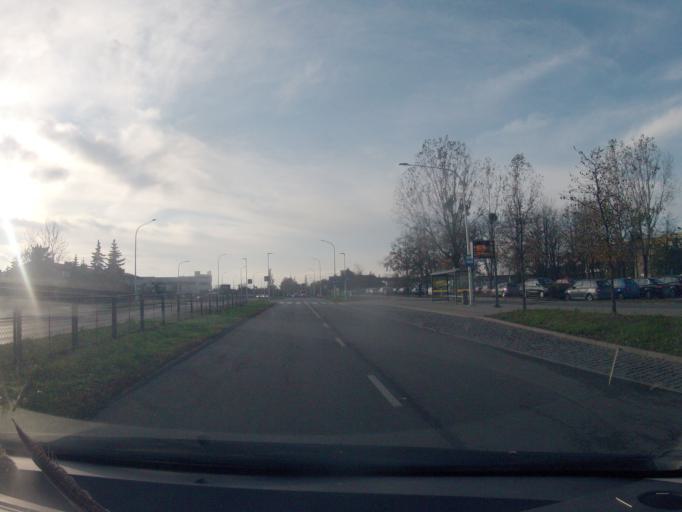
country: PL
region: Opole Voivodeship
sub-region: Powiat opolski
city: Opole
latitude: 50.6728
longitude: 17.9532
